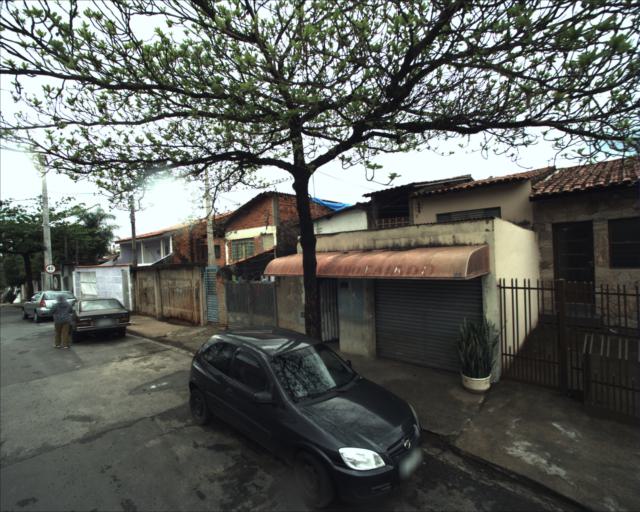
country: BR
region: Sao Paulo
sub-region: Sorocaba
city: Sorocaba
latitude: -23.5031
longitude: -47.5040
